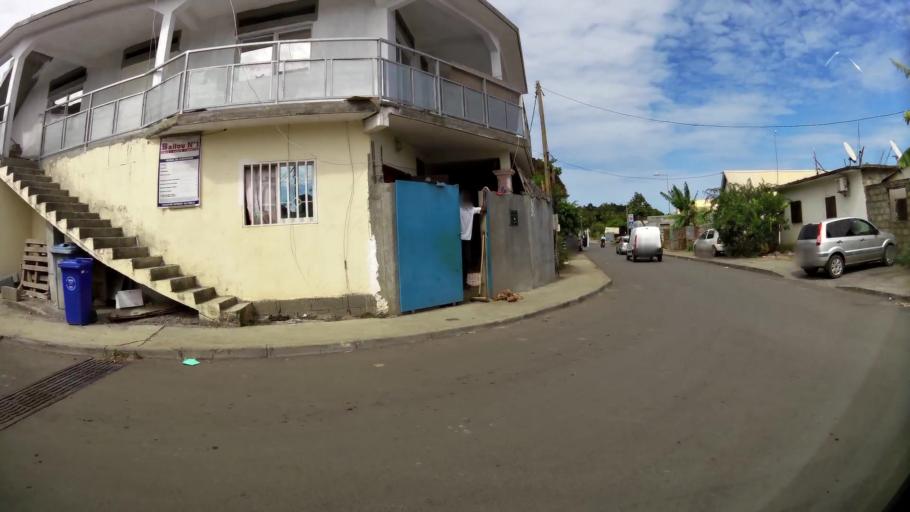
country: YT
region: Mamoudzou
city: Mamoudzou
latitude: -12.7819
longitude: 45.2335
